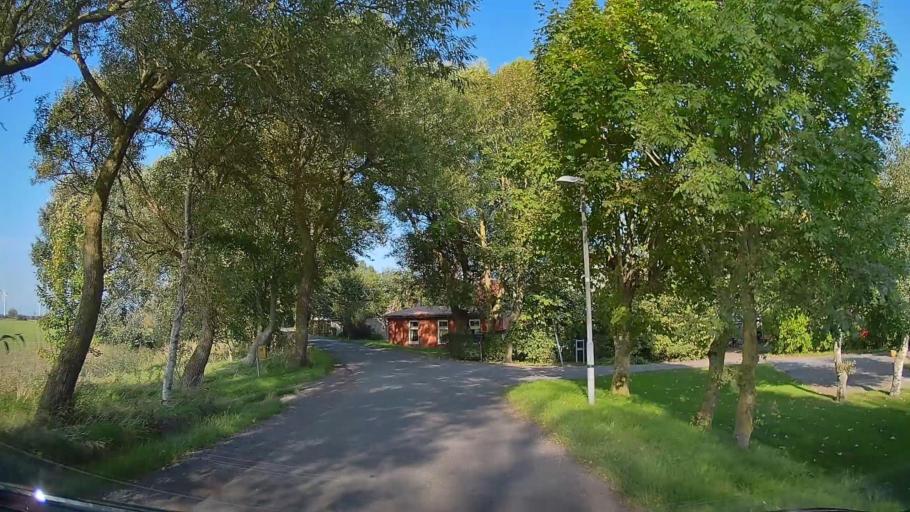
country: DE
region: Lower Saxony
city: Padingbuttel
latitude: 53.7156
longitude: 8.5174
